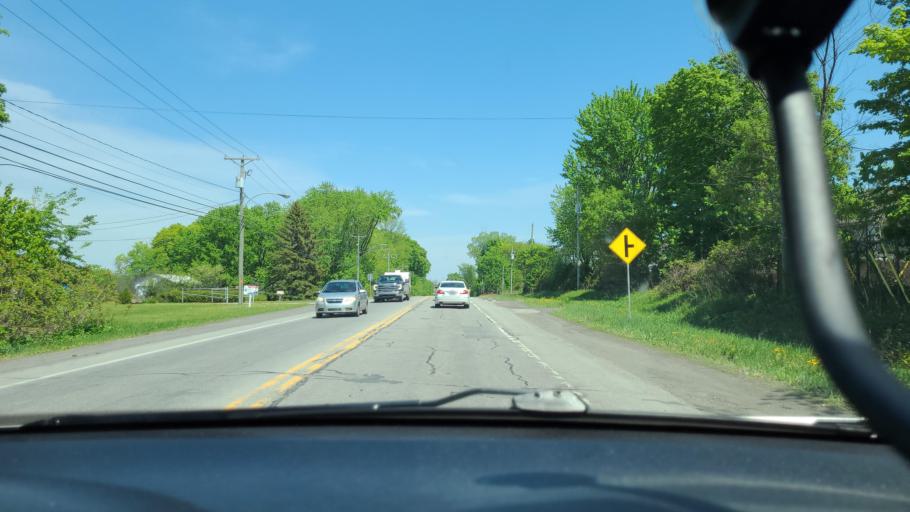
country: CA
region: Quebec
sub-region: Laurentides
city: Saint-Eustache
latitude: 45.5862
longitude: -73.9371
